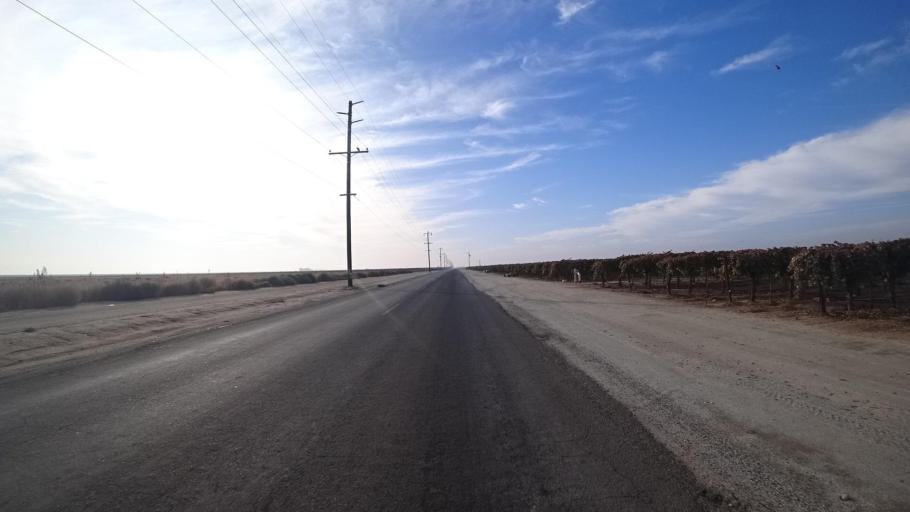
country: US
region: California
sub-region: Kern County
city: Delano
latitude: 35.7420
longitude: -119.2053
